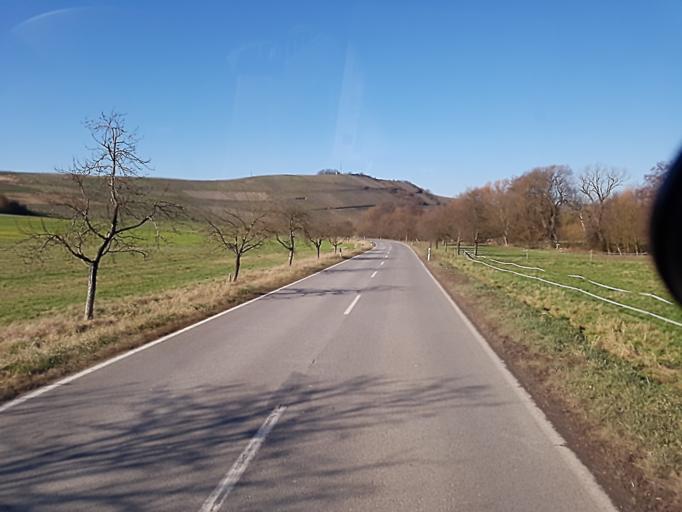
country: DE
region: Rheinland-Pfalz
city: Veldenz
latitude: 49.8928
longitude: 7.0178
